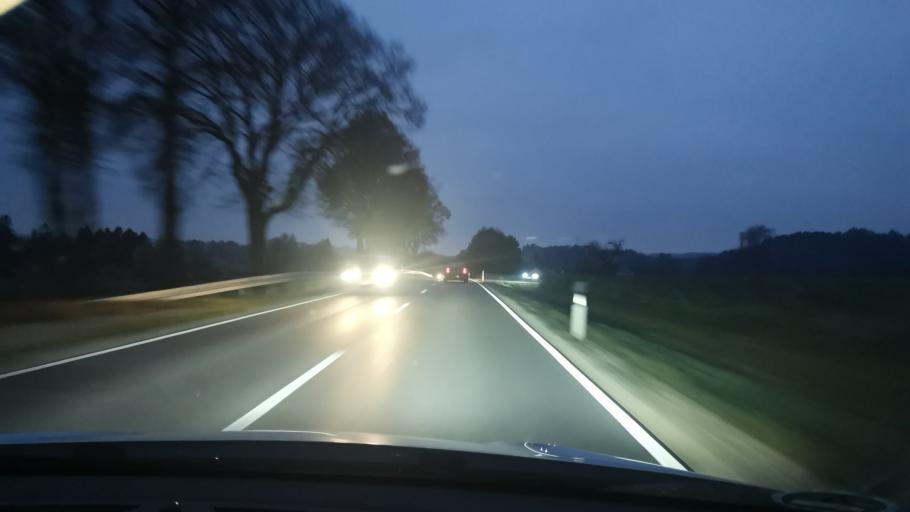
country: DE
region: Bavaria
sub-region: Swabia
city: Pottmes
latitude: 48.5727
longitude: 11.0765
